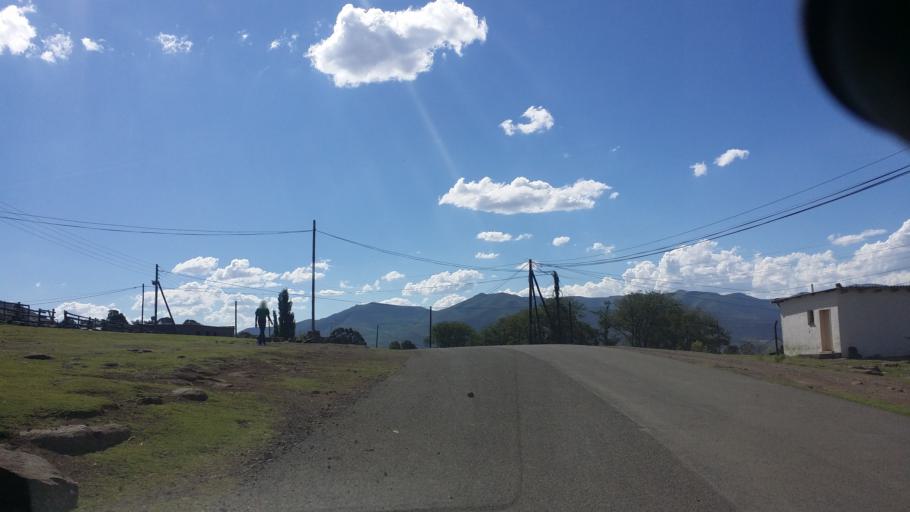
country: LS
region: Mokhotlong
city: Mokhotlong
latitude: -29.2902
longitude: 29.0698
